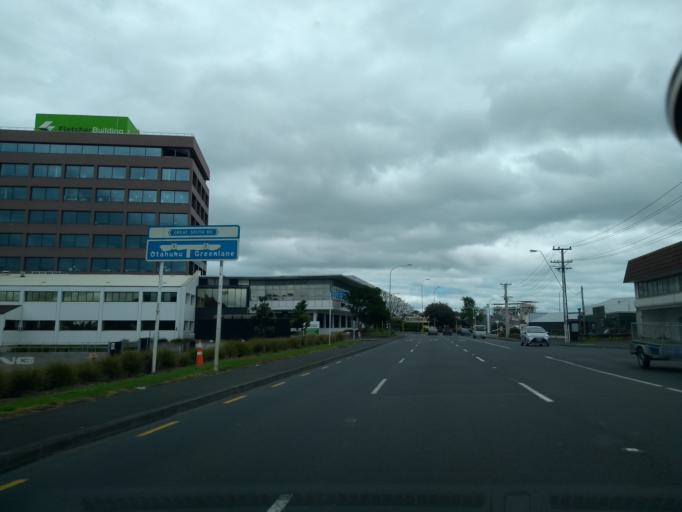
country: NZ
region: Auckland
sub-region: Auckland
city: Tamaki
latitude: -36.9104
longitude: 174.8191
